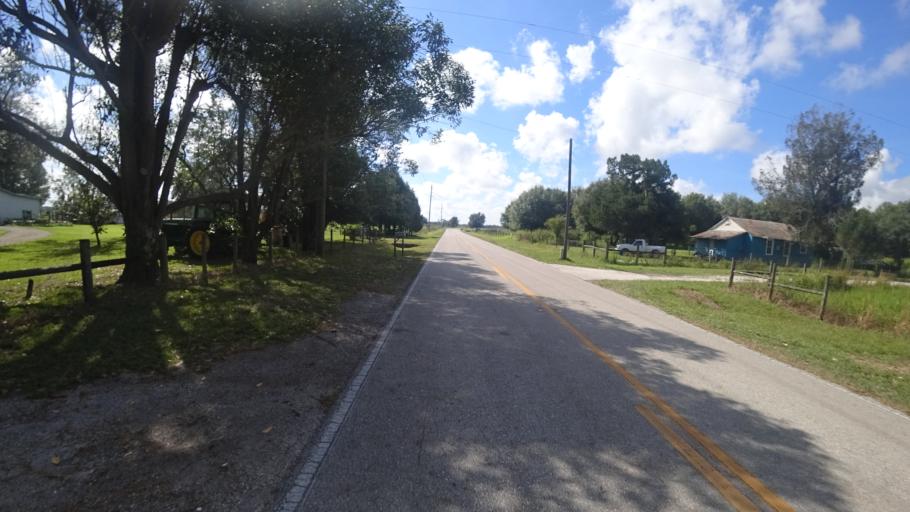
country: US
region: Florida
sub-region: Sarasota County
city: Lake Sarasota
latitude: 27.3704
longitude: -82.2193
